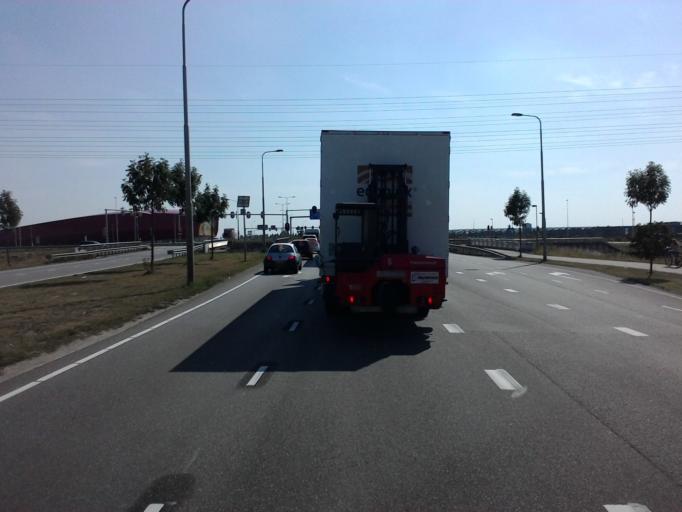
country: NL
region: Utrecht
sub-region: Stichtse Vecht
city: Maarssen
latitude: 52.1113
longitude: 5.0540
